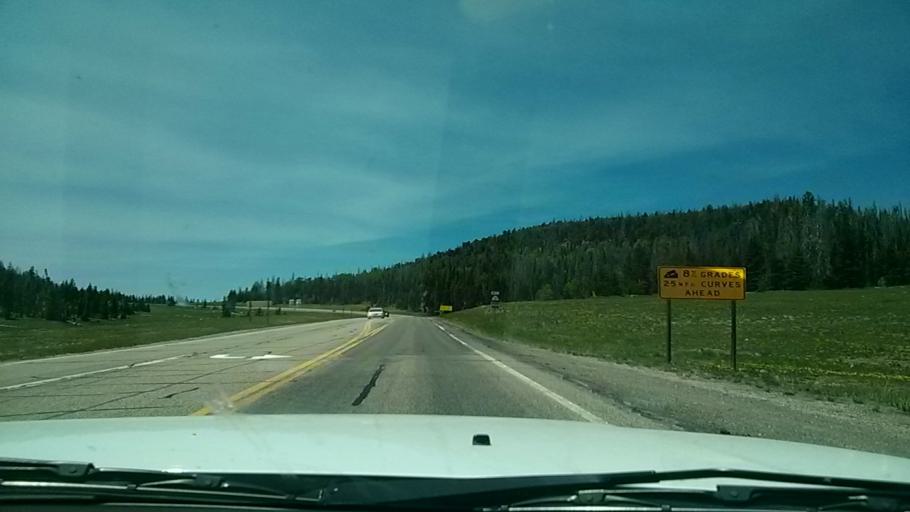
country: US
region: Utah
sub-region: Iron County
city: Cedar City
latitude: 37.5720
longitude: -112.8366
